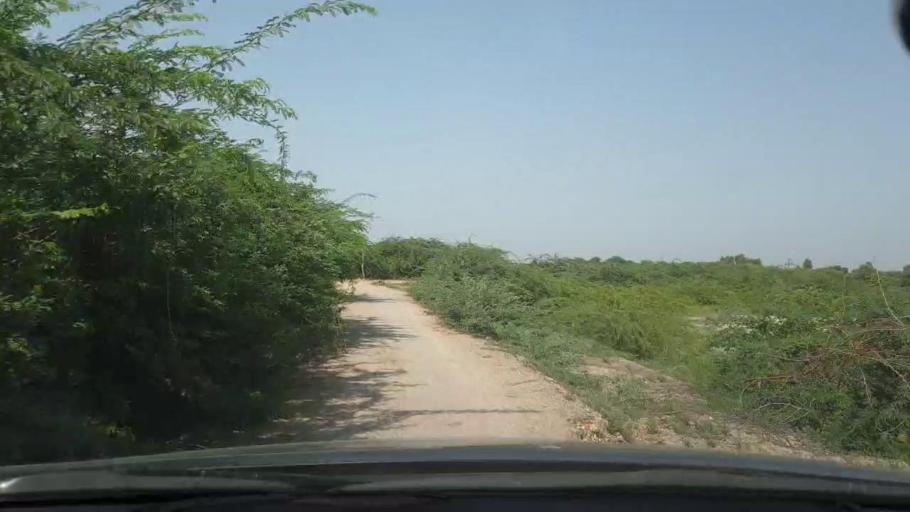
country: PK
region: Sindh
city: Naukot
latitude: 24.8125
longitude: 69.2720
